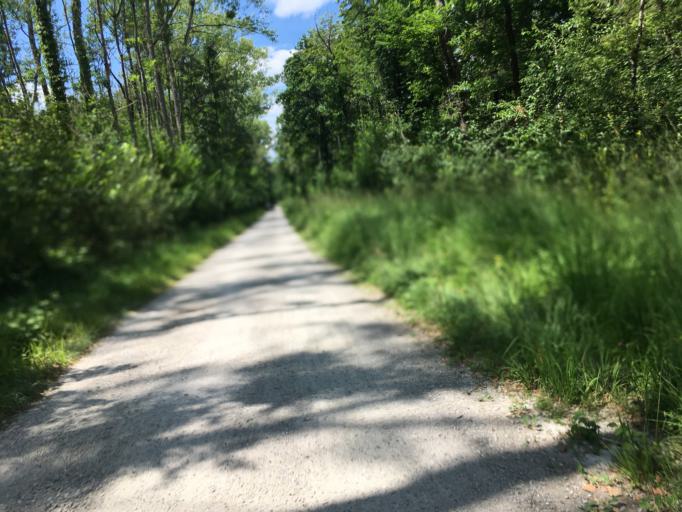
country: CH
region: Neuchatel
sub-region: Neuchatel District
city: Neuchatel
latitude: 46.9103
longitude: 6.9425
